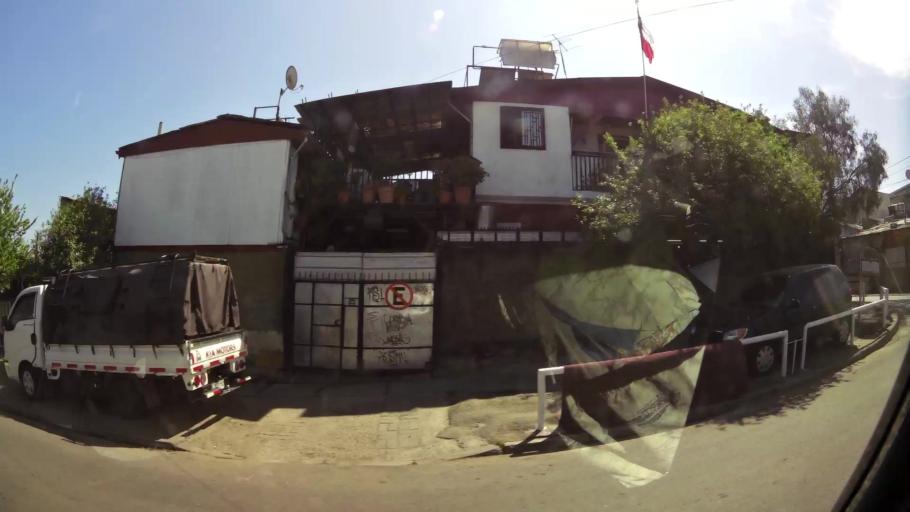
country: CL
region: Santiago Metropolitan
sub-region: Provincia de Santiago
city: Lo Prado
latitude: -33.4900
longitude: -70.7256
